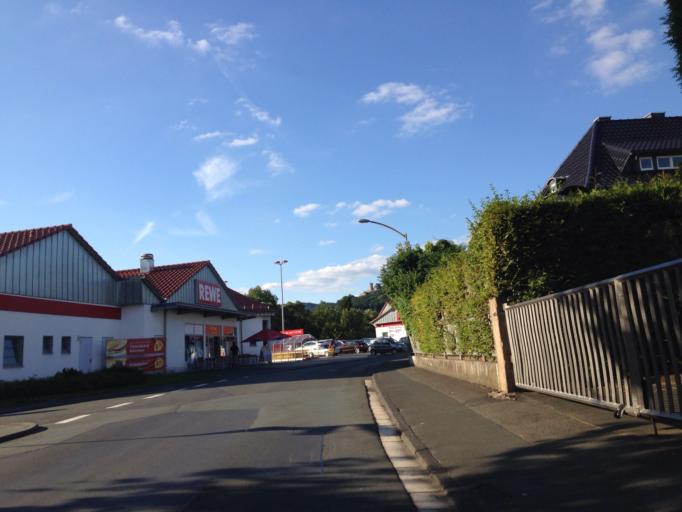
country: DE
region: Hesse
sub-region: Regierungsbezirk Giessen
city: Biedenkopf
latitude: 50.9043
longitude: 8.5334
